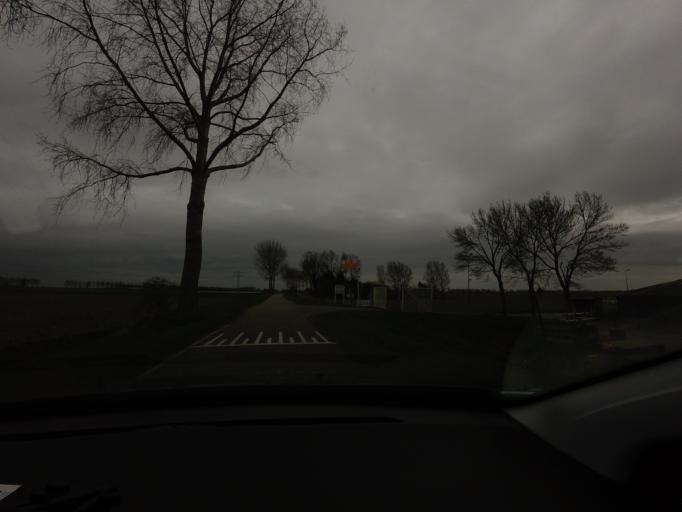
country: NL
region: South Holland
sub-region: Gemeente Goeree-Overflakkee
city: Middelharnis
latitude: 51.7290
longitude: 4.2247
